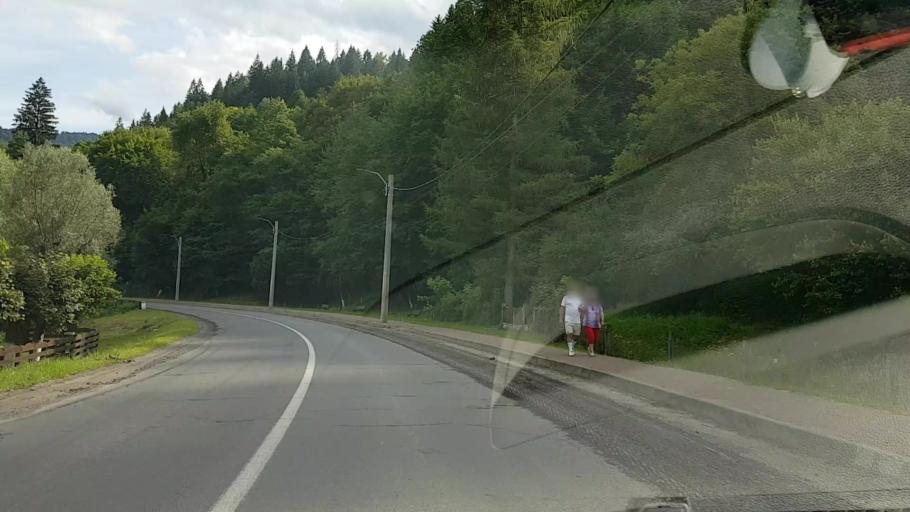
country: RO
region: Neamt
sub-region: Comuna Bicaz
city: Dodeni
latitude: 46.9186
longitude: 26.0845
